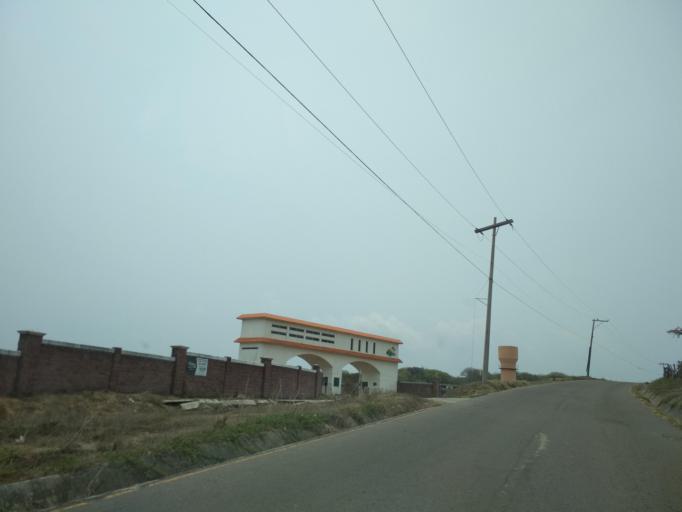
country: MX
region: Veracruz
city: Anton Lizardo
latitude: 19.0487
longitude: -96.0306
